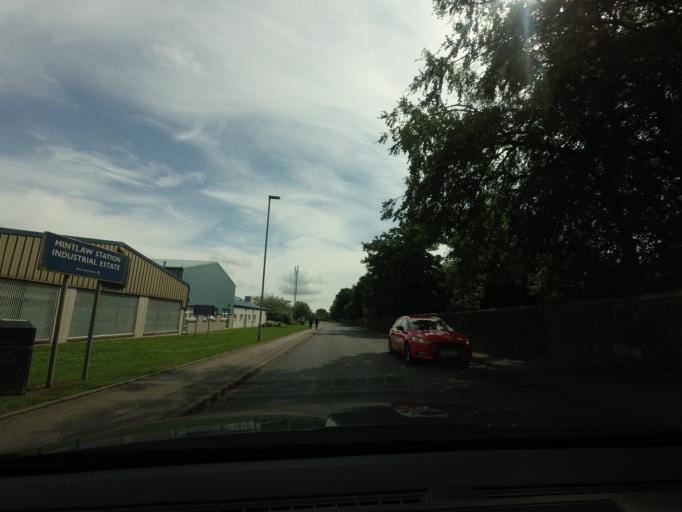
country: GB
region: Scotland
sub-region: Aberdeenshire
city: Mintlaw
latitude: 57.5257
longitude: -2.0173
